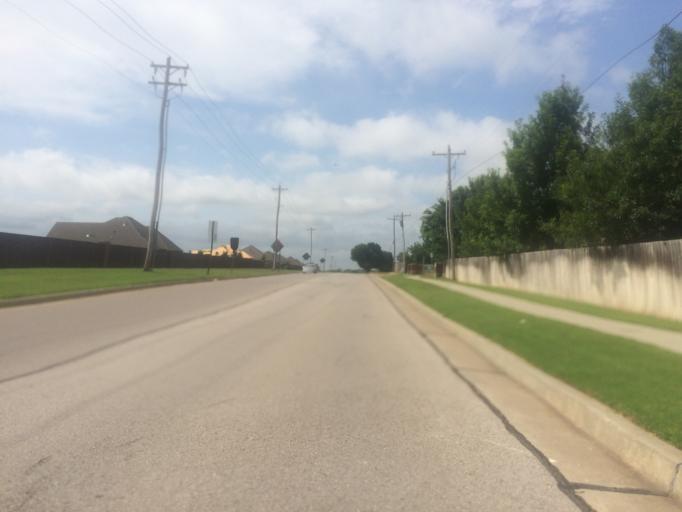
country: US
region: Oklahoma
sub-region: Cleveland County
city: Noble
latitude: 35.1729
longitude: -97.4237
